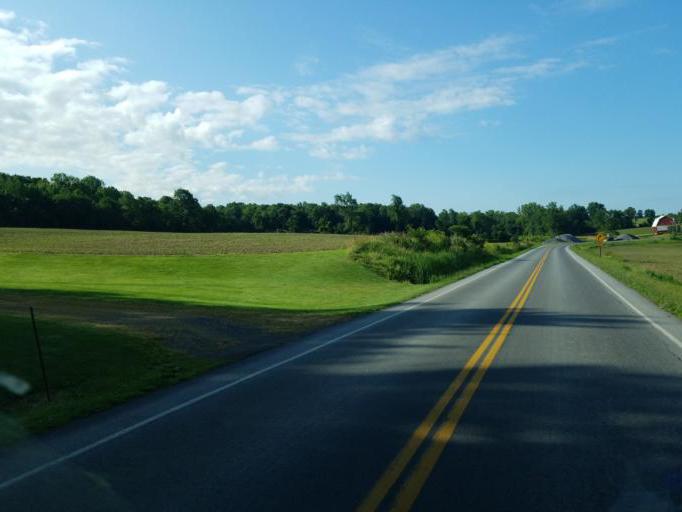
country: US
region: New York
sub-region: Wayne County
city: Clyde
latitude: 43.0387
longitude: -76.9049
